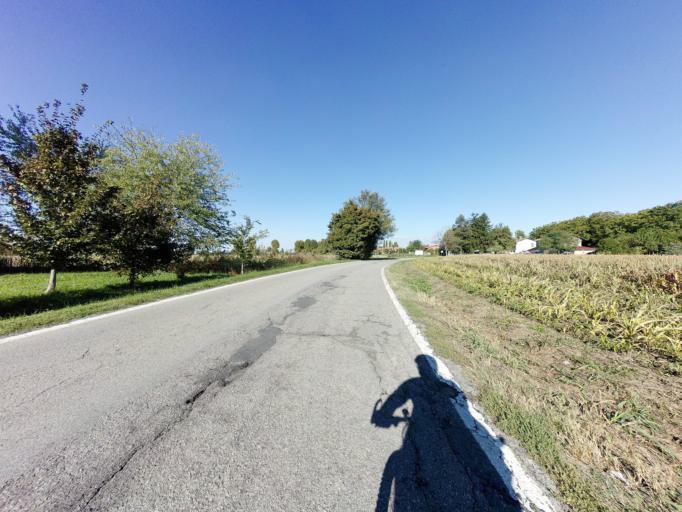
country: IT
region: Emilia-Romagna
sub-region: Provincia di Bologna
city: Progresso
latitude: 44.5670
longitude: 11.3894
